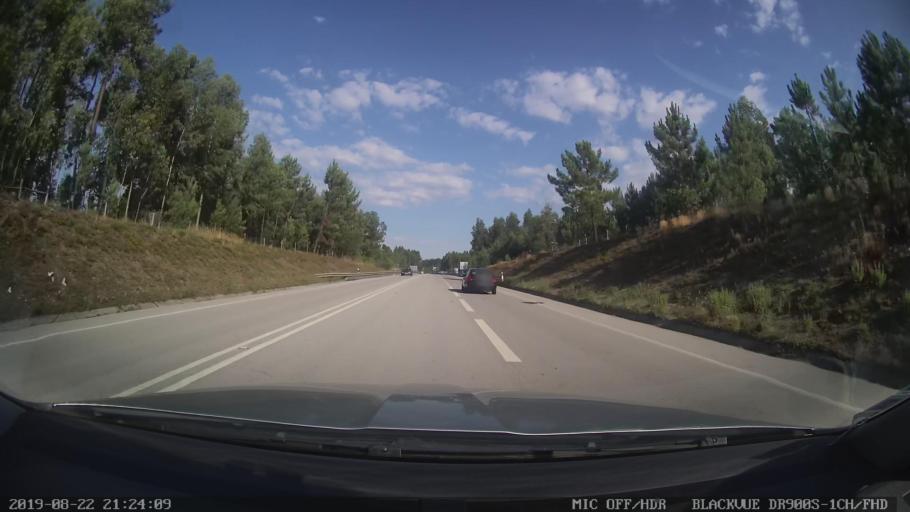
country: PT
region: Castelo Branco
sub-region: Serta
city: Serta
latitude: 39.8385
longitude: -8.1181
